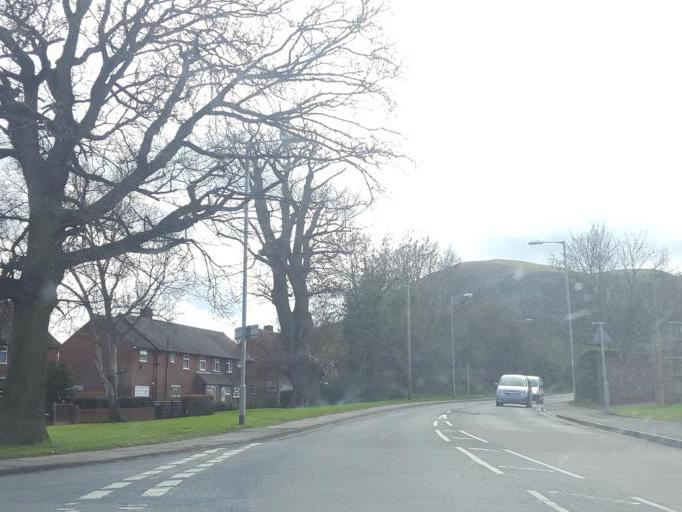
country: GB
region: England
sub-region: Worcestershire
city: Great Malvern
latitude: 52.1326
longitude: -2.3303
